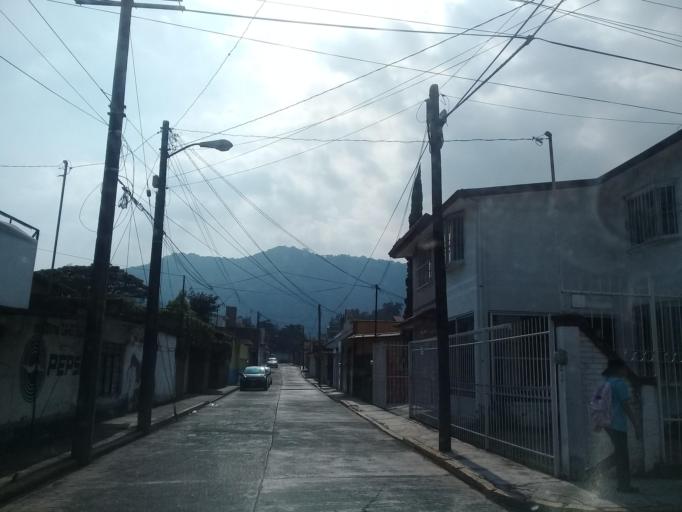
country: MX
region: Veracruz
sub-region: Ixhuatlancillo
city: Union y Progreso
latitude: 18.8663
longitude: -97.1098
